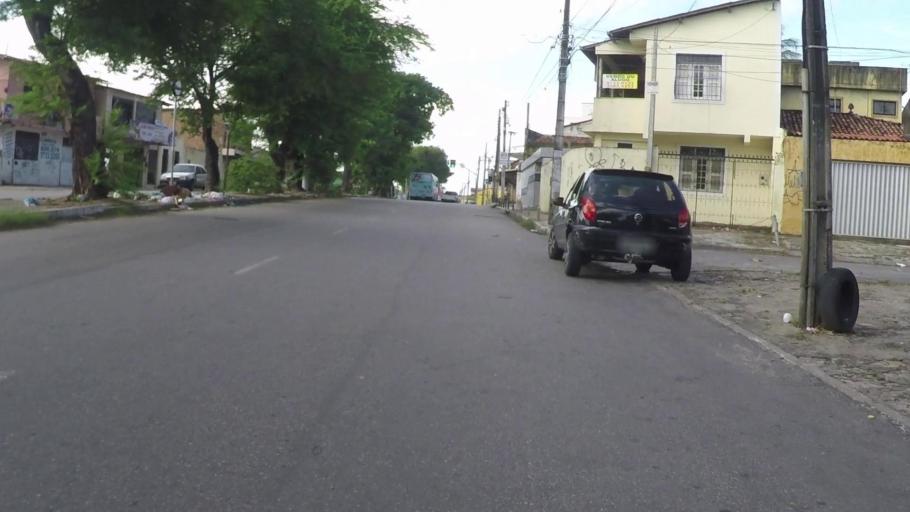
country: BR
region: Ceara
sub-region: Fortaleza
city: Fortaleza
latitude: -3.7166
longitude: -38.5883
